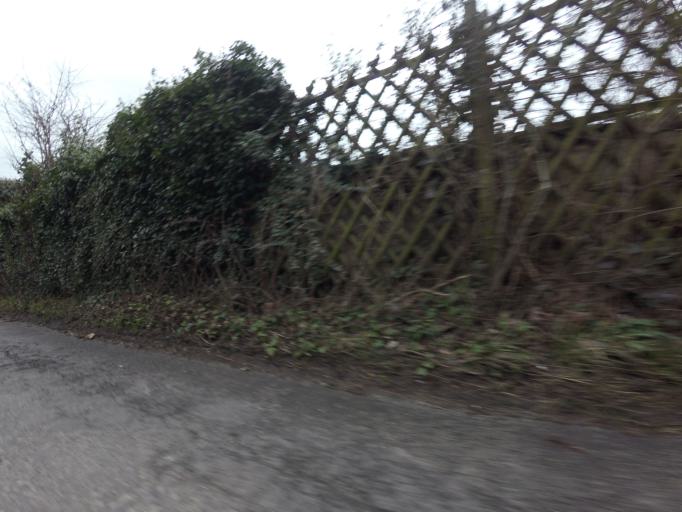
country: GB
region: England
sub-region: Greater London
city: Orpington
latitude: 51.3872
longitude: 0.1307
